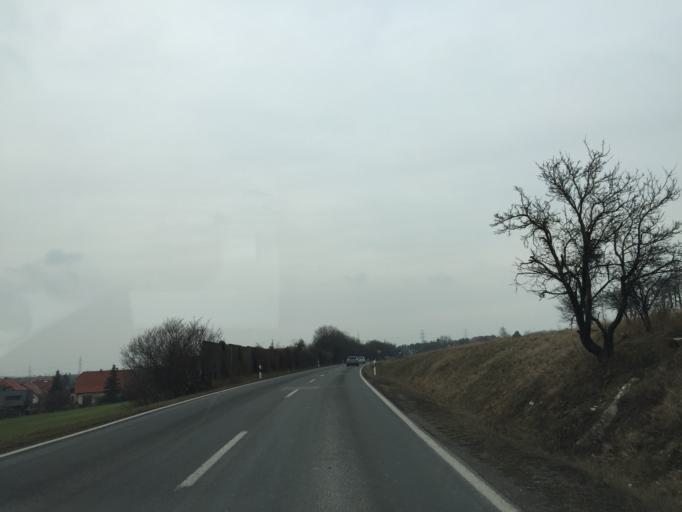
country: DE
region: Thuringia
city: Klettbach
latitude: 50.9124
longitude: 11.1582
